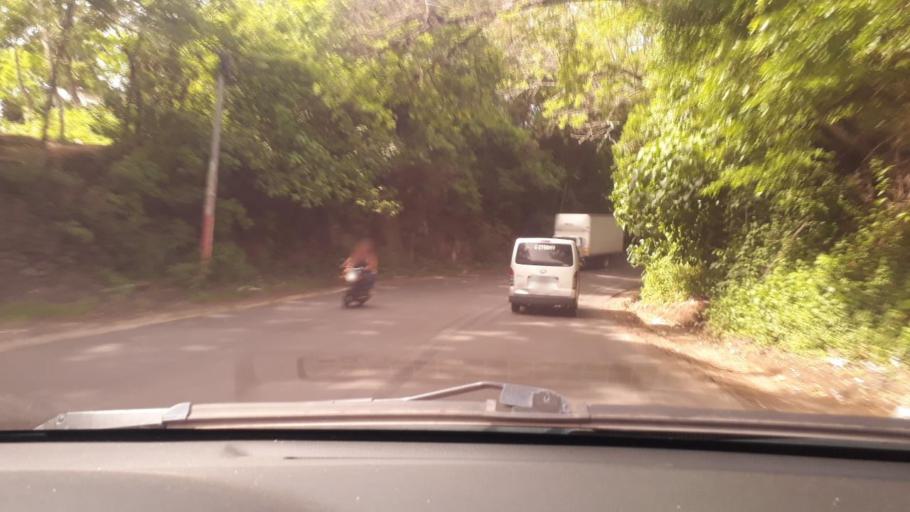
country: GT
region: Jutiapa
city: Quesada
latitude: 14.2721
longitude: -90.0041
